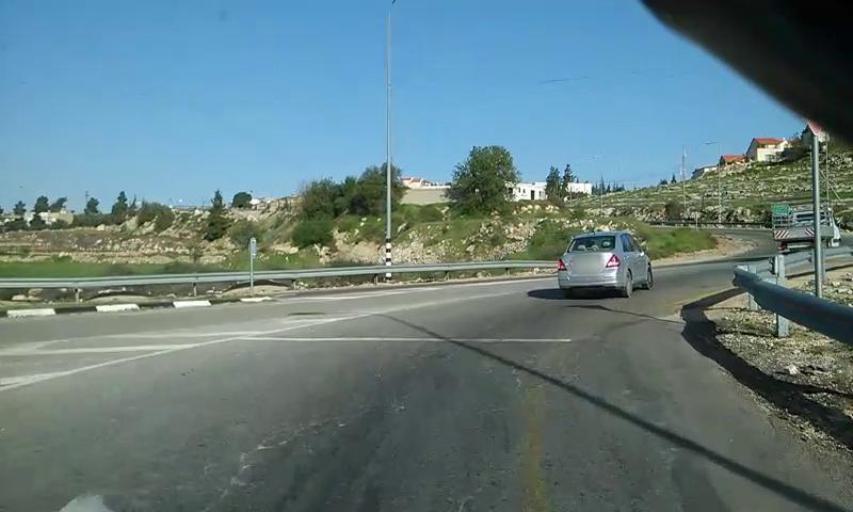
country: PS
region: West Bank
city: Qalqas
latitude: 31.4950
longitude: 35.0775
